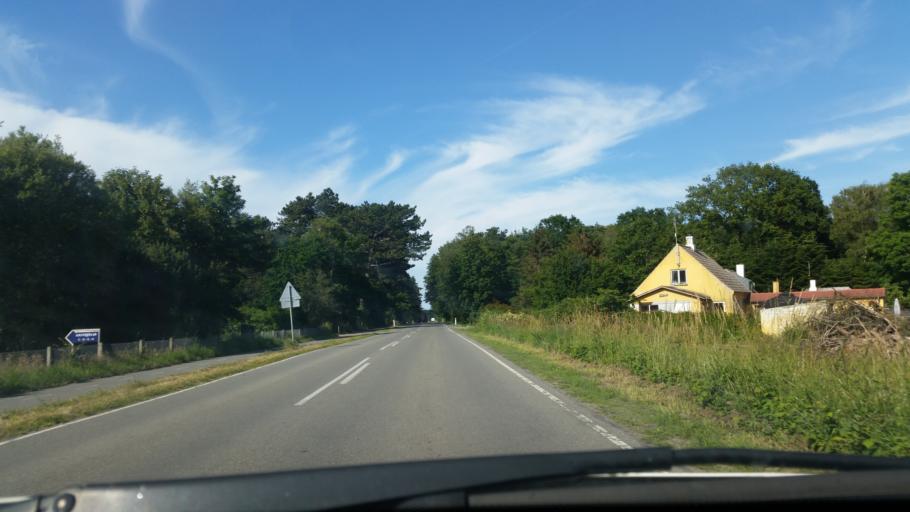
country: DK
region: Central Jutland
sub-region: Samso Kommune
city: Tranebjerg
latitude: 55.8631
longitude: 10.5783
